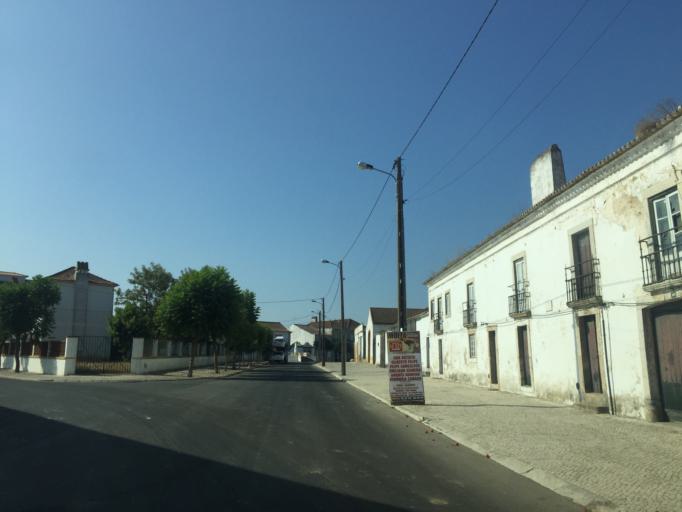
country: PT
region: Santarem
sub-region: Salvaterra de Magos
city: Salvaterra de Magos
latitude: 39.0304
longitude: -8.7948
